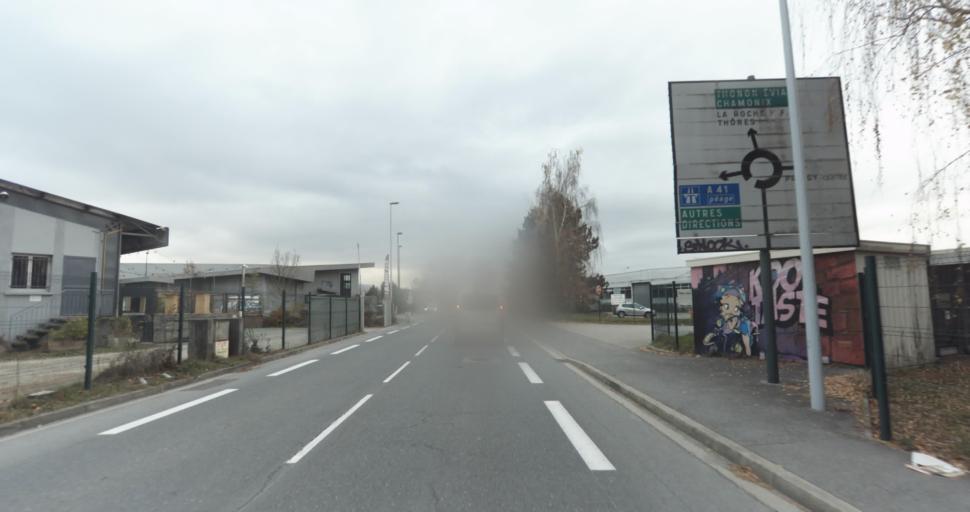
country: FR
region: Rhone-Alpes
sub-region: Departement de la Haute-Savoie
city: Pringy
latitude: 45.9390
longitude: 6.1270
